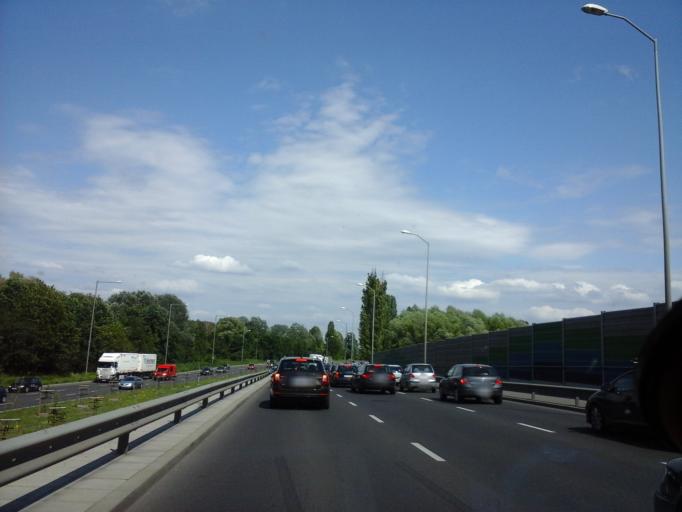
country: PL
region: West Pomeranian Voivodeship
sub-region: Szczecin
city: Szczecin
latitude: 53.3867
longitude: 14.6353
